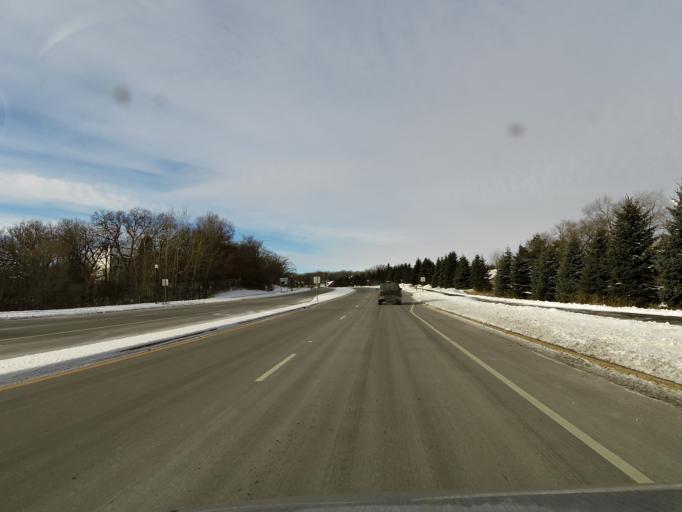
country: US
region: Minnesota
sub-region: Dakota County
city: Burnsville
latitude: 44.7151
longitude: -93.2919
